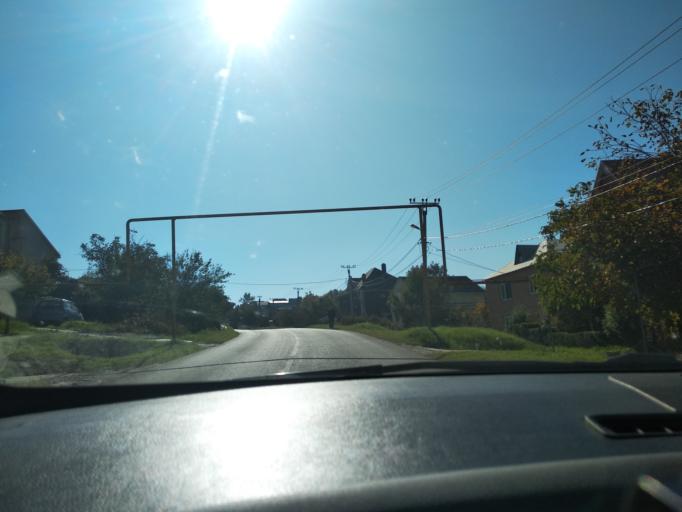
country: RU
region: Krasnodarskiy
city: Goryachiy Klyuch
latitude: 44.6275
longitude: 39.1568
